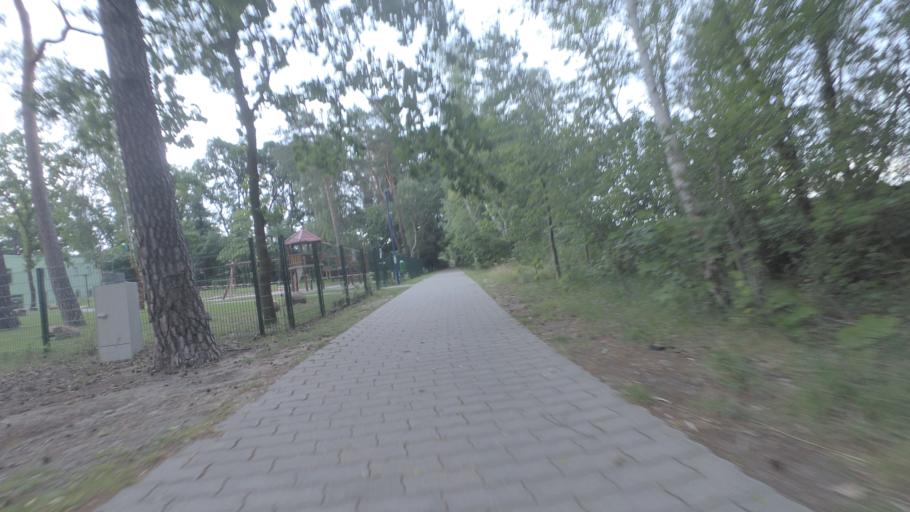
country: DE
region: Brandenburg
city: Bestensee
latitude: 52.2365
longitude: 13.6644
